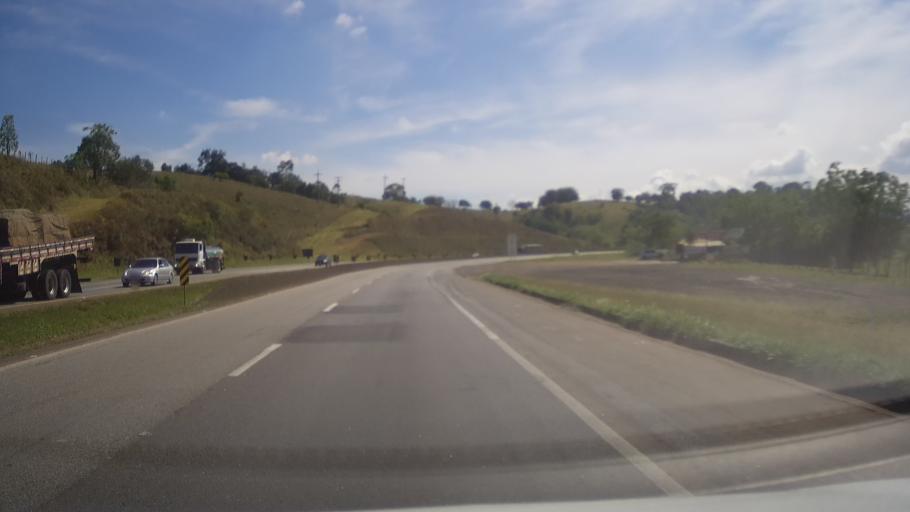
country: BR
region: Minas Gerais
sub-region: Cambui
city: Cambui
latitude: -22.5354
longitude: -46.0351
